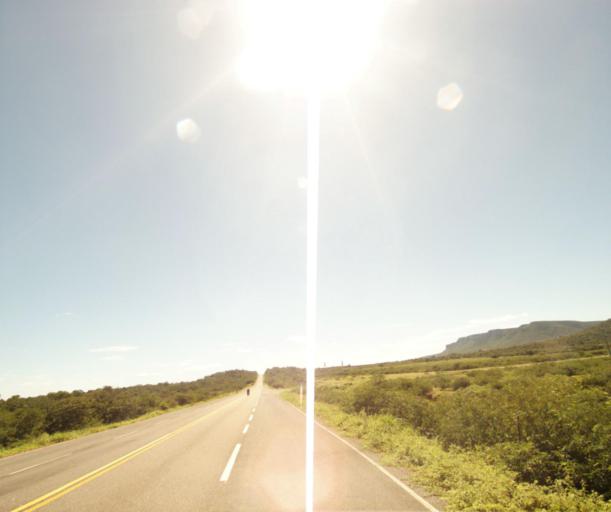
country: BR
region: Bahia
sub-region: Palmas De Monte Alto
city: Palmas de Monte Alto
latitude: -14.2513
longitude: -43.1845
